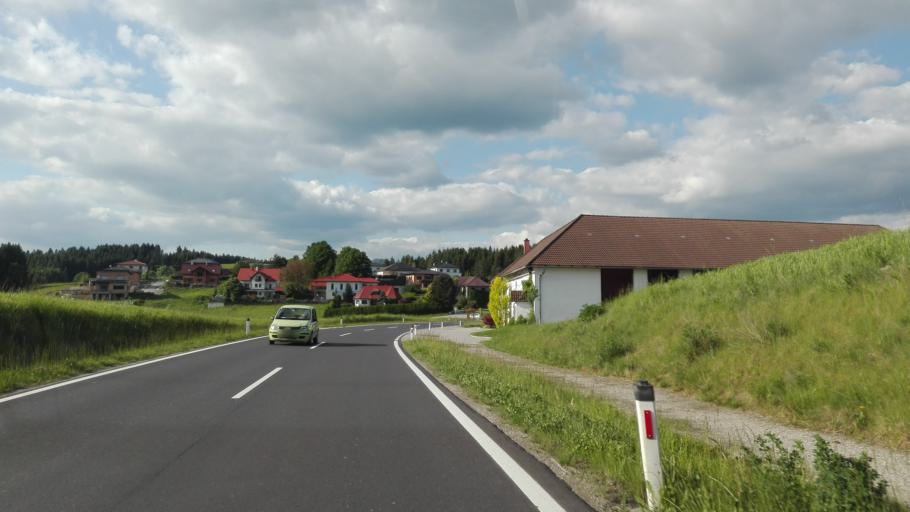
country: AT
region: Upper Austria
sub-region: Politischer Bezirk Perg
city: Perg
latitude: 48.3577
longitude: 14.6802
